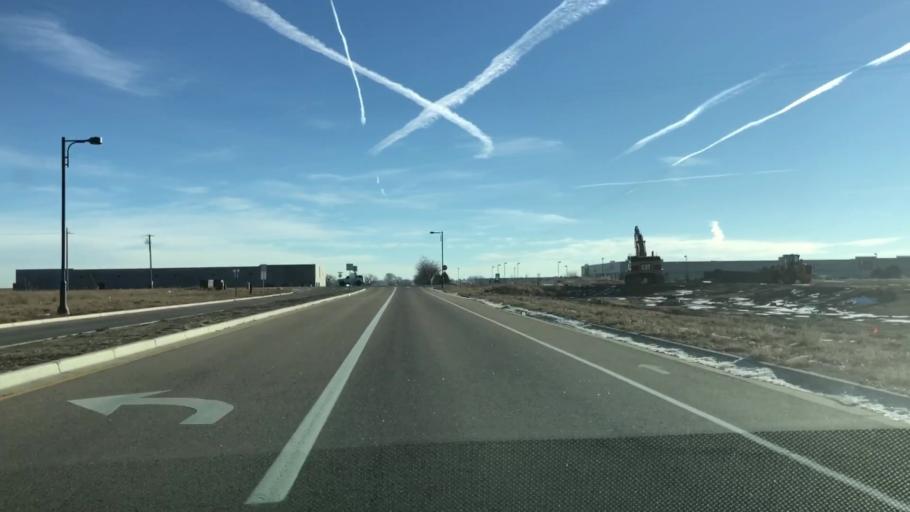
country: US
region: Colorado
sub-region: Weld County
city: Johnstown
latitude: 40.4036
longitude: -104.9660
